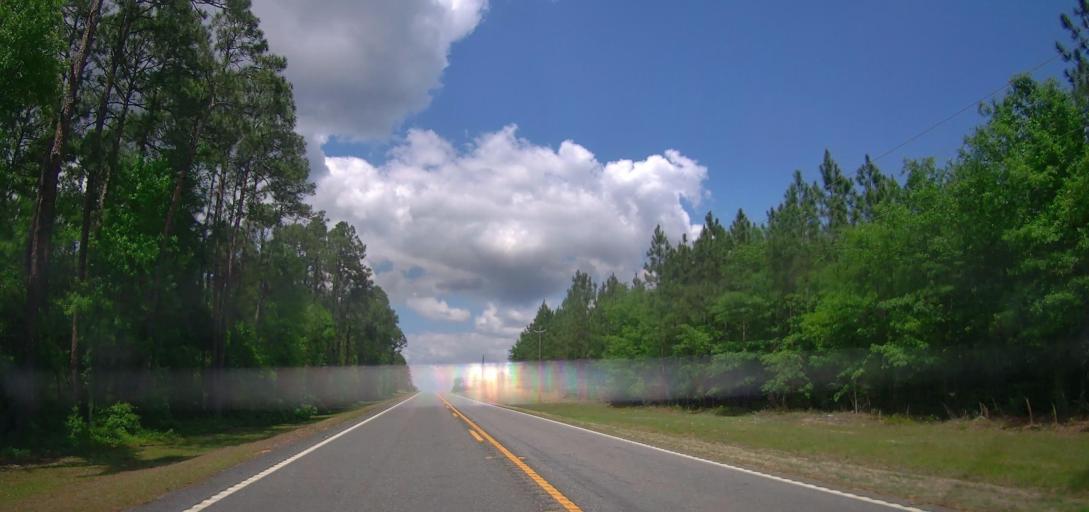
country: US
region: Georgia
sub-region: Treutlen County
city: Soperton
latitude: 32.4184
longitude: -82.6083
